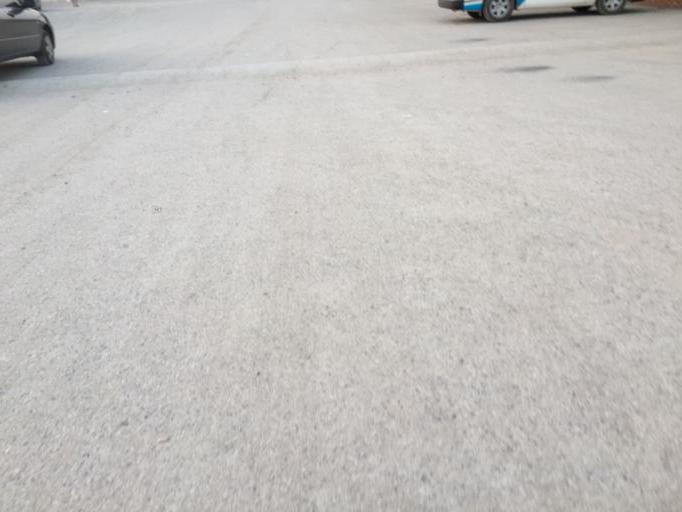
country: AE
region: Ra's al Khaymah
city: Ras al-Khaimah
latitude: 25.7929
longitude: 55.9735
